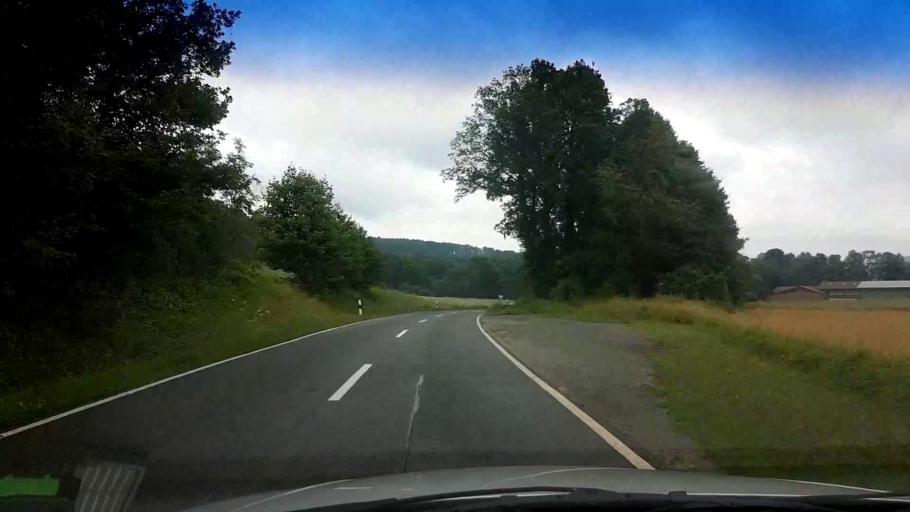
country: DE
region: Bavaria
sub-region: Upper Franconia
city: Weismain
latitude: 50.0722
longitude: 11.2226
